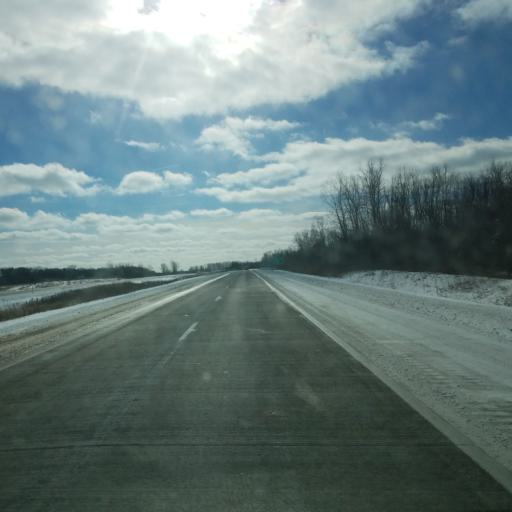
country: US
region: Michigan
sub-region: Clinton County
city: DeWitt
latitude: 42.8335
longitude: -84.5191
